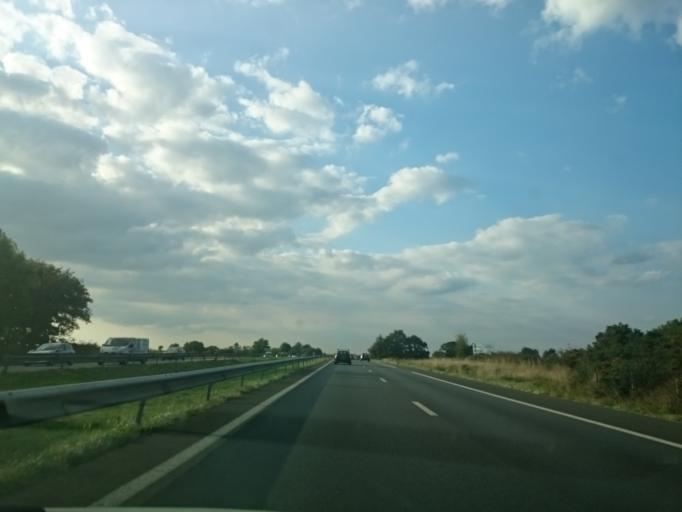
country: FR
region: Pays de la Loire
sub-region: Departement de la Loire-Atlantique
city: Vigneux-de-Bretagne
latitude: 47.3074
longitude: -1.7624
